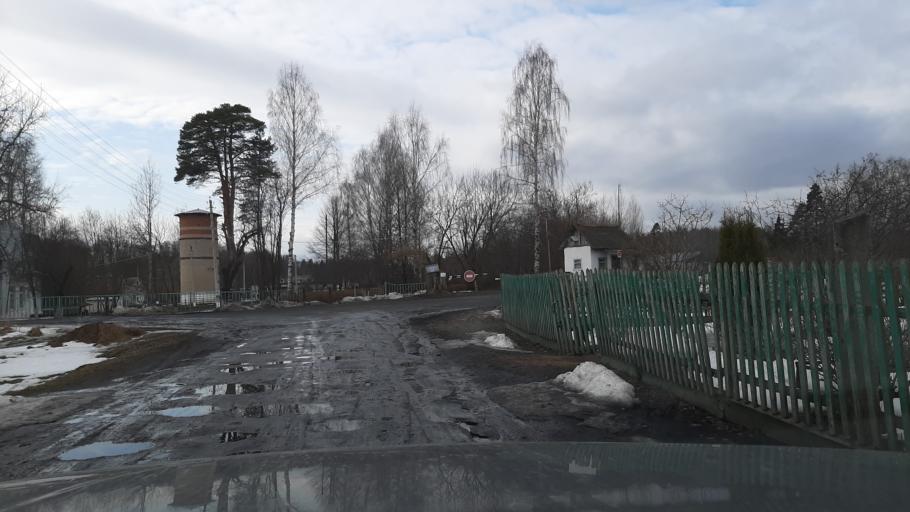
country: RU
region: Ivanovo
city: Teykovo
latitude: 56.8981
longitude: 40.6648
